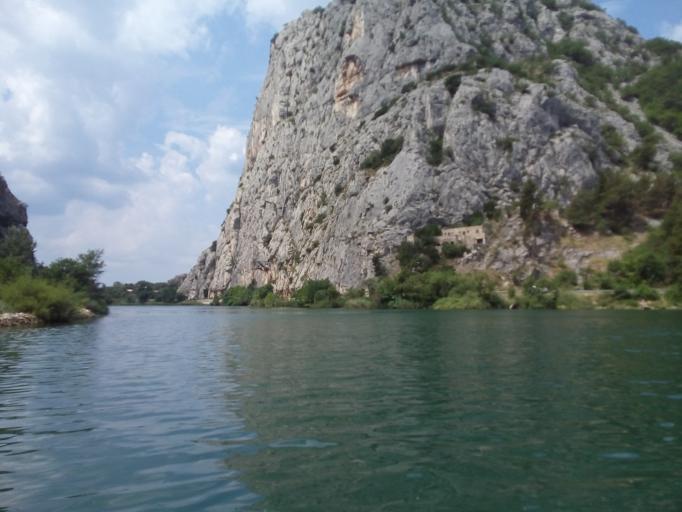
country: HR
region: Splitsko-Dalmatinska
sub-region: Grad Omis
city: Omis
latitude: 43.4515
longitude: 16.6966
